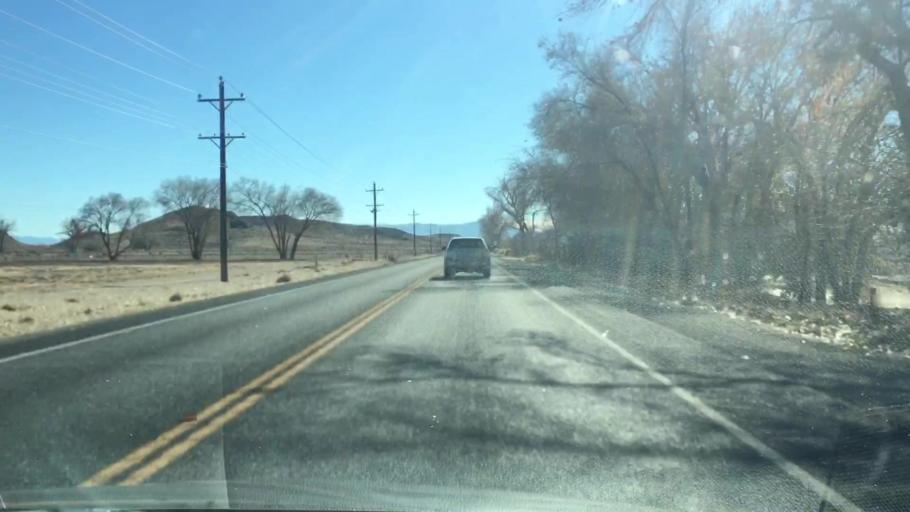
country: US
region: Nevada
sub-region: Lyon County
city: Yerington
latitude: 39.0315
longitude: -119.1816
